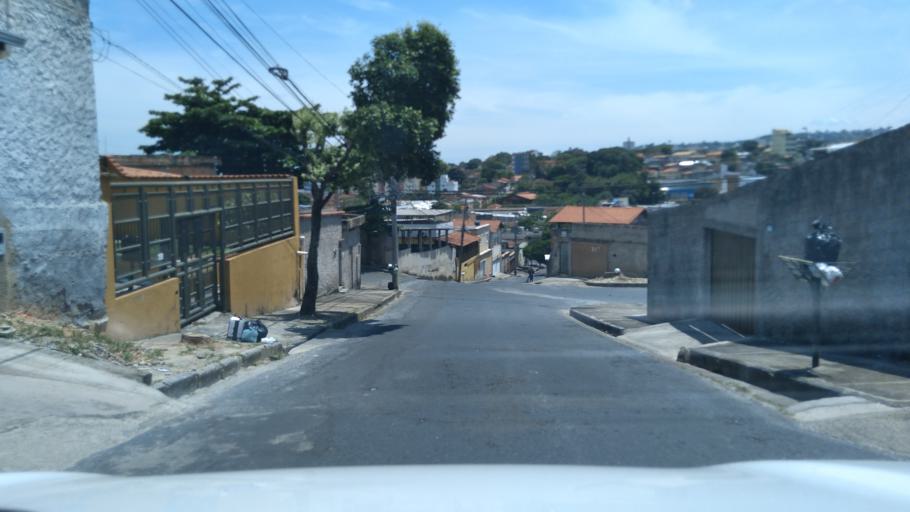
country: BR
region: Minas Gerais
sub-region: Contagem
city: Contagem
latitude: -19.9000
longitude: -44.0115
